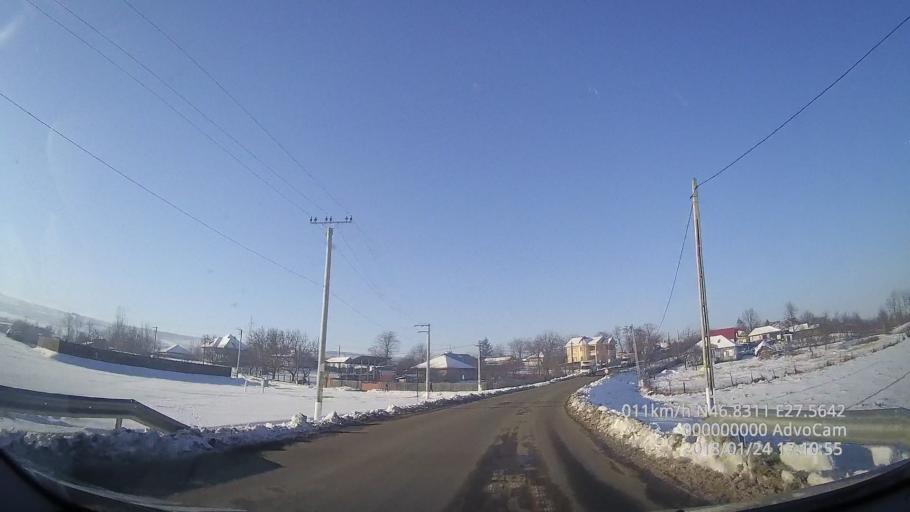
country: RO
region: Vaslui
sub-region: Comuna Vulturesti
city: Vulturesti
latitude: 46.8313
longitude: 27.5640
